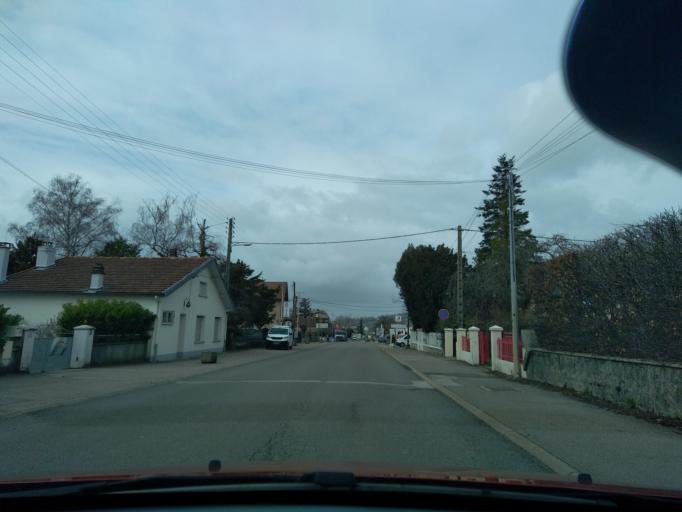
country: FR
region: Franche-Comte
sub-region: Departement du Jura
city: Perrigny
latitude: 46.6678
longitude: 5.5777
